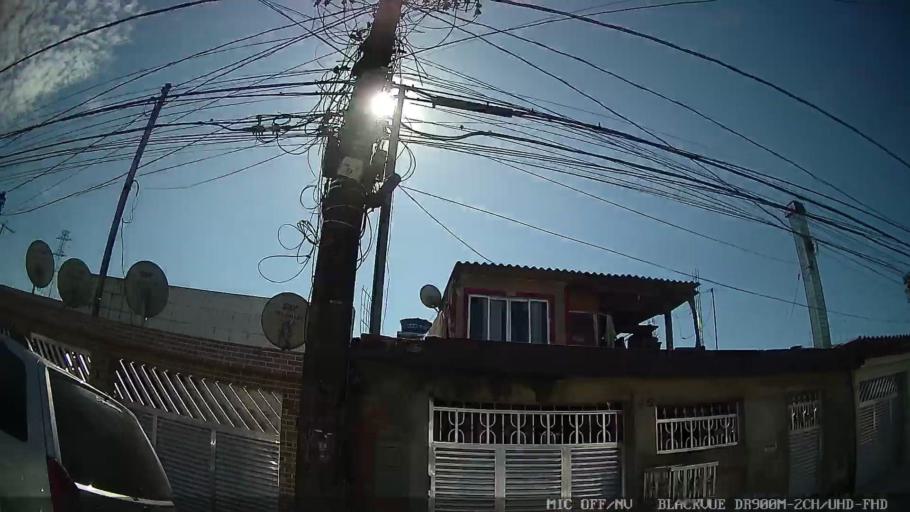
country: BR
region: Sao Paulo
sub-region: Guaruja
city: Guaruja
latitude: -23.9525
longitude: -46.2802
